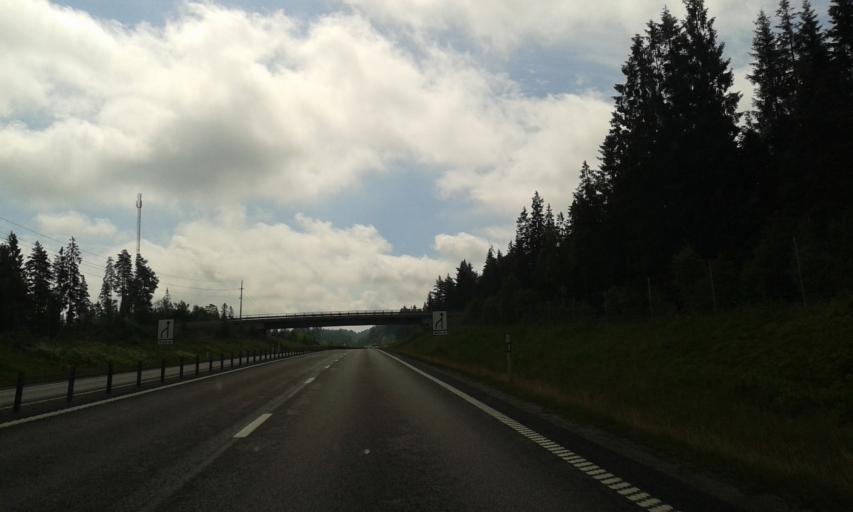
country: SE
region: Vaestra Goetaland
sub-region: Boras Kommun
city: Ganghester
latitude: 57.6655
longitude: 13.0337
